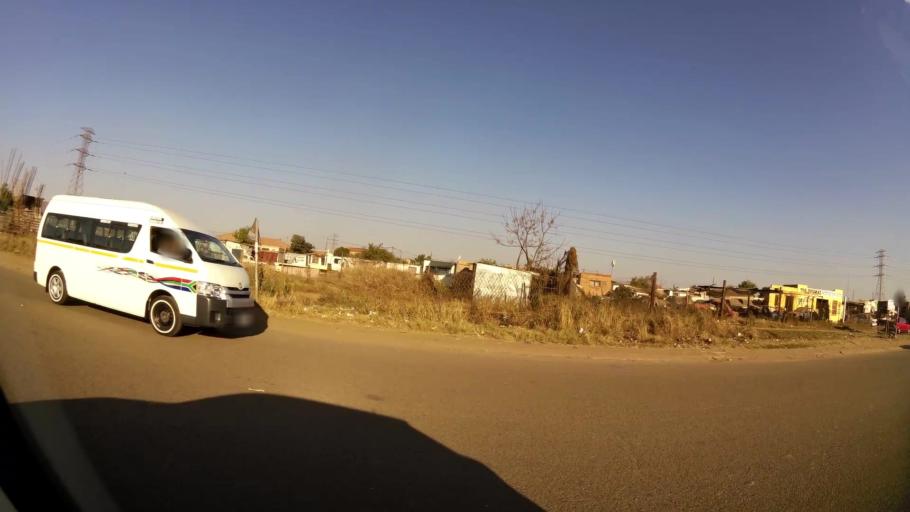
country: ZA
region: Gauteng
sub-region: City of Tshwane Metropolitan Municipality
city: Cullinan
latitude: -25.7130
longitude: 28.4059
